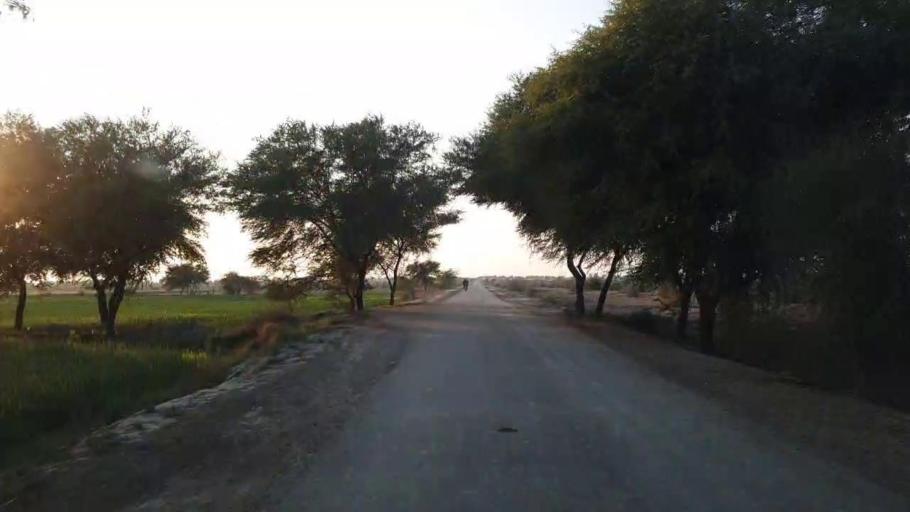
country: PK
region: Sindh
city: Shahpur Chakar
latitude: 26.1565
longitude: 68.5534
